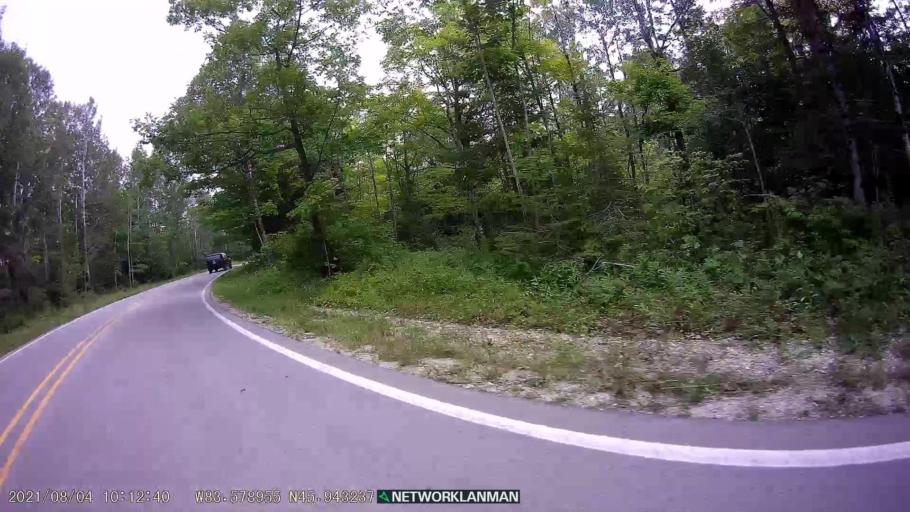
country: CA
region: Ontario
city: Thessalon
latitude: 45.9433
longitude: -83.5794
